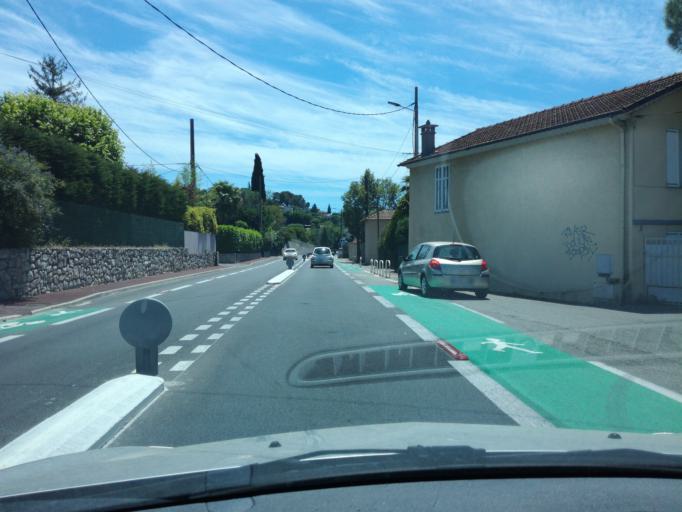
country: FR
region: Provence-Alpes-Cote d'Azur
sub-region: Departement des Alpes-Maritimes
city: Mougins
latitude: 43.5925
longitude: 7.0019
